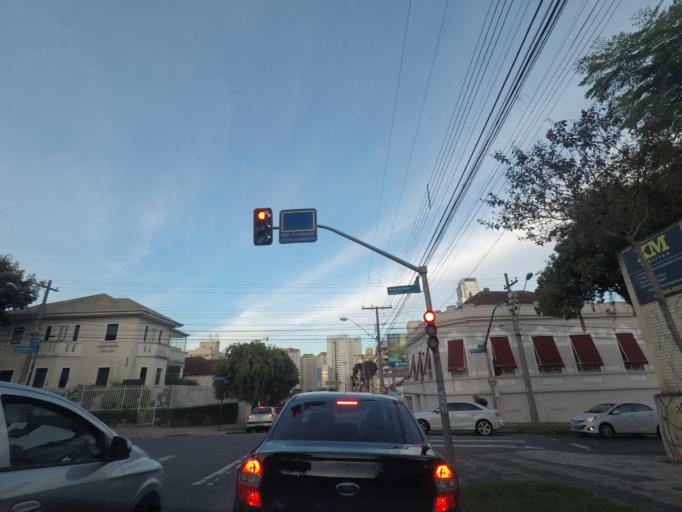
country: BR
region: Parana
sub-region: Curitiba
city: Curitiba
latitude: -25.4221
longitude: -49.2726
